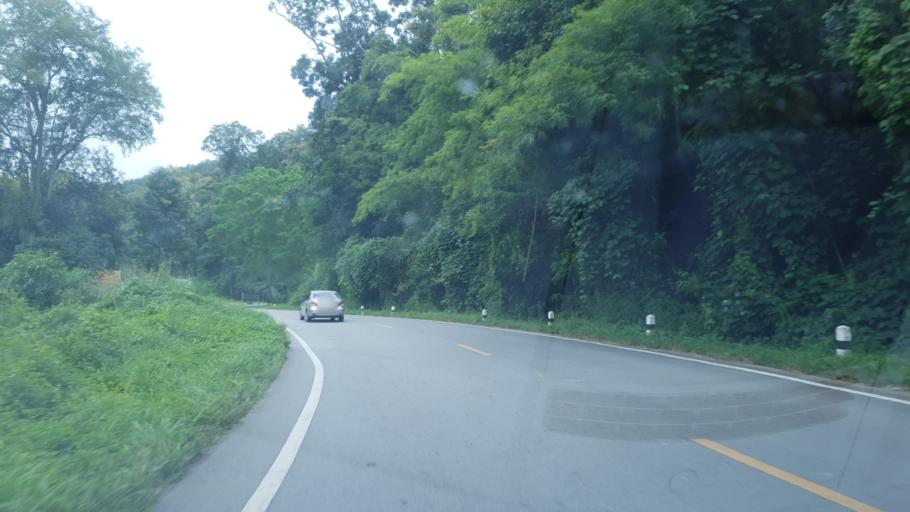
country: TH
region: Mae Hong Son
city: Khun Yuam
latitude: 18.7245
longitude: 97.9083
